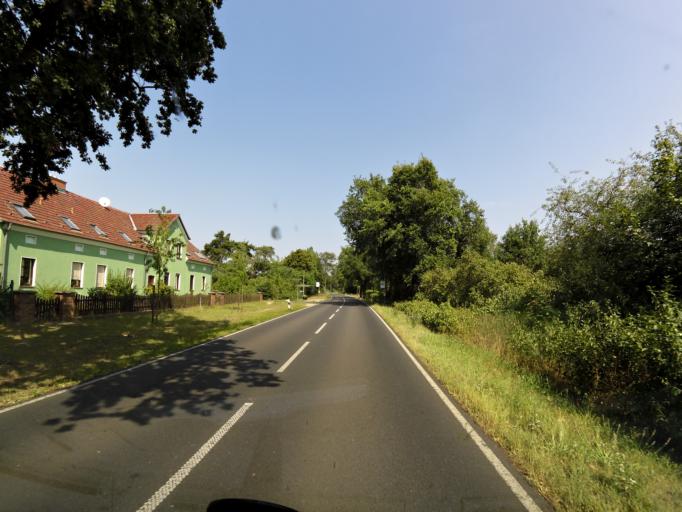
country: DE
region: Brandenburg
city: Liebenwalde
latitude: 52.8519
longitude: 13.3292
